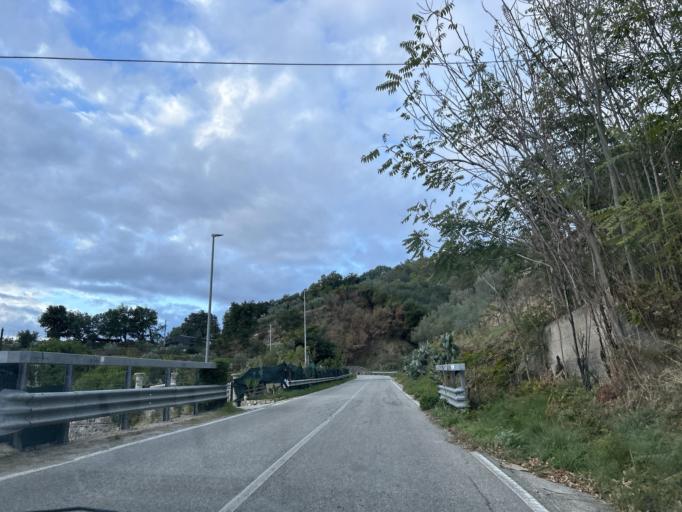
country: IT
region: Calabria
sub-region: Provincia di Catanzaro
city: Montauro
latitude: 38.7481
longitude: 16.5098
